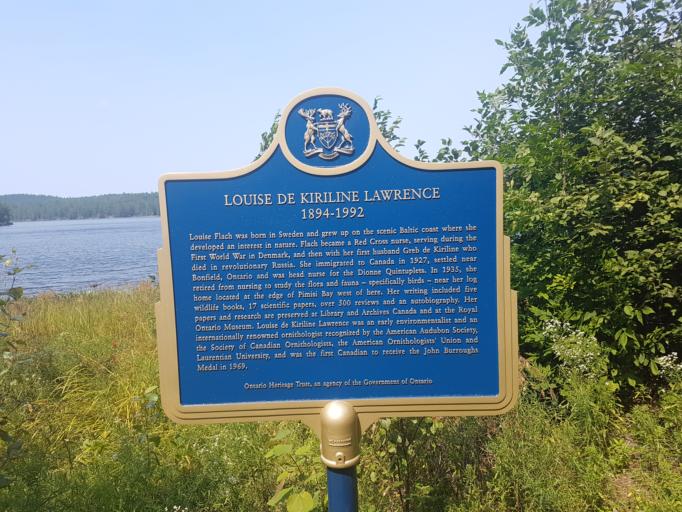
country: CA
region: Ontario
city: Mattawa
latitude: 46.2719
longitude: -78.9789
